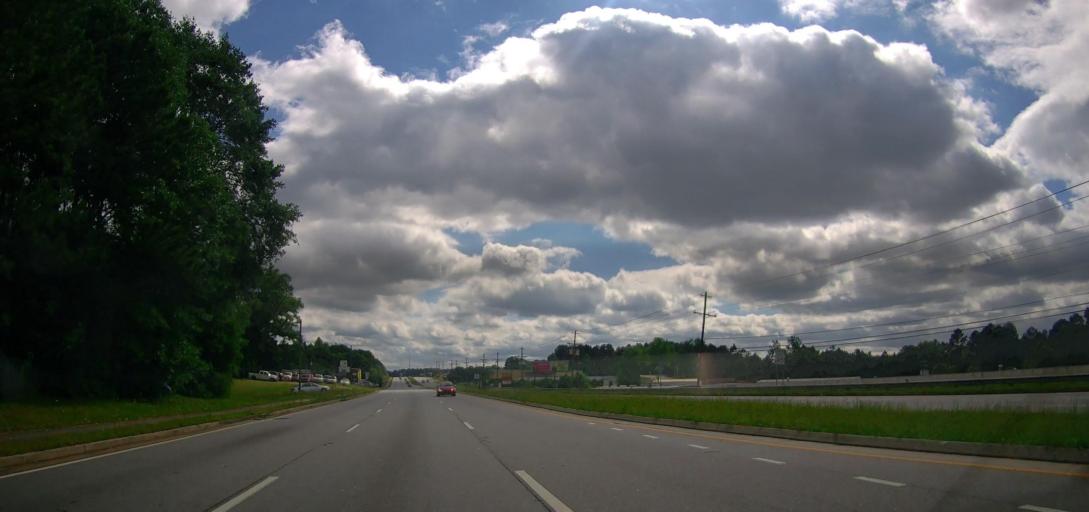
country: US
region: Georgia
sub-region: Rockdale County
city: Conyers
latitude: 33.6683
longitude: -83.9886
